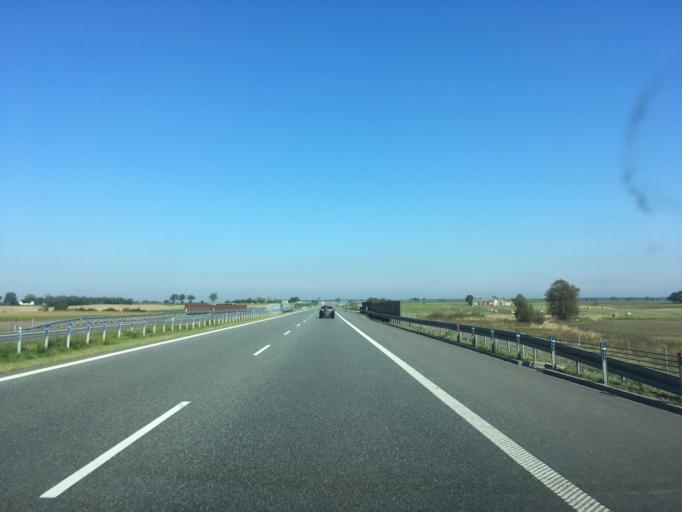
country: PL
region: Kujawsko-Pomorskie
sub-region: Powiat torunski
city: Lubicz Dolny
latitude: 53.1142
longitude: 18.7444
